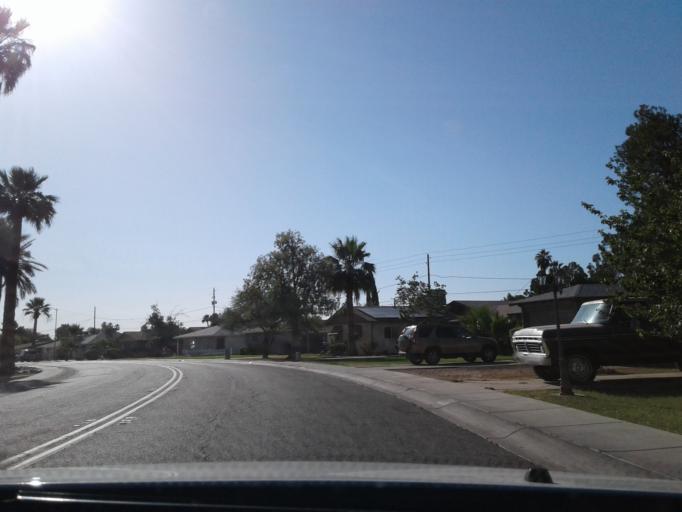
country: US
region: Arizona
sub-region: Maricopa County
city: Phoenix
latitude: 33.5018
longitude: -112.0888
